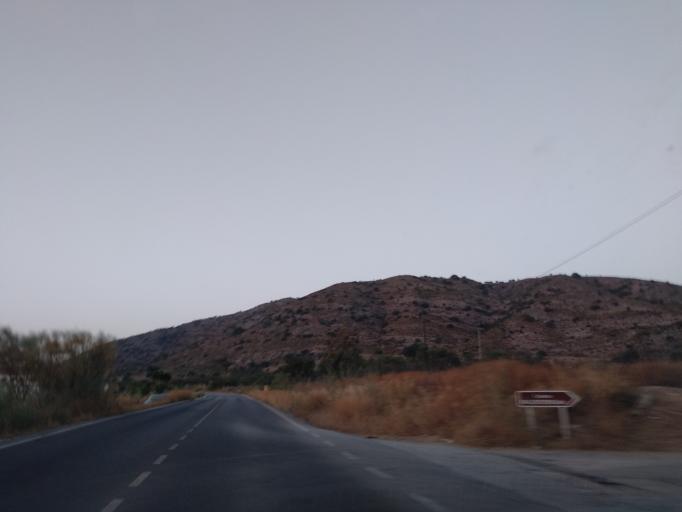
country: ES
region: Andalusia
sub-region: Provincia de Malaga
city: Cartama
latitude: 36.6883
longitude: -4.6517
